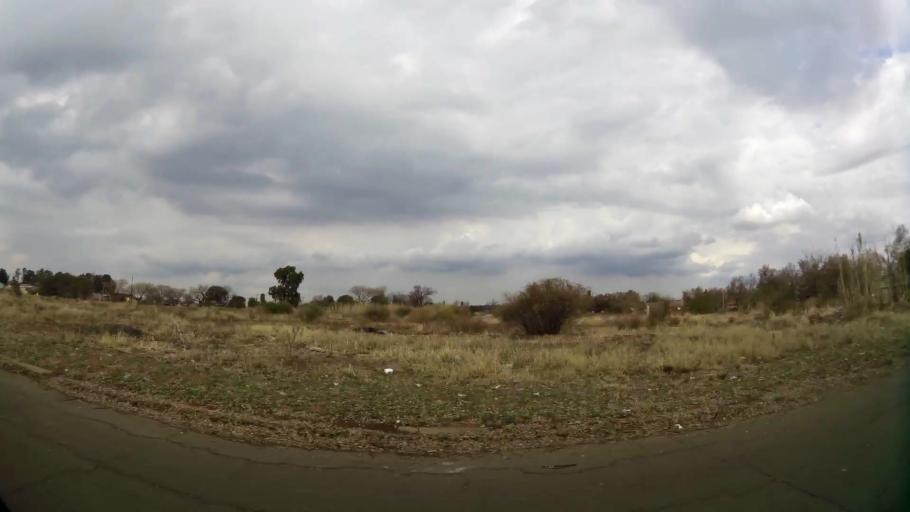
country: ZA
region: Gauteng
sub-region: Sedibeng District Municipality
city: Vanderbijlpark
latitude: -26.7040
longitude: 27.8046
